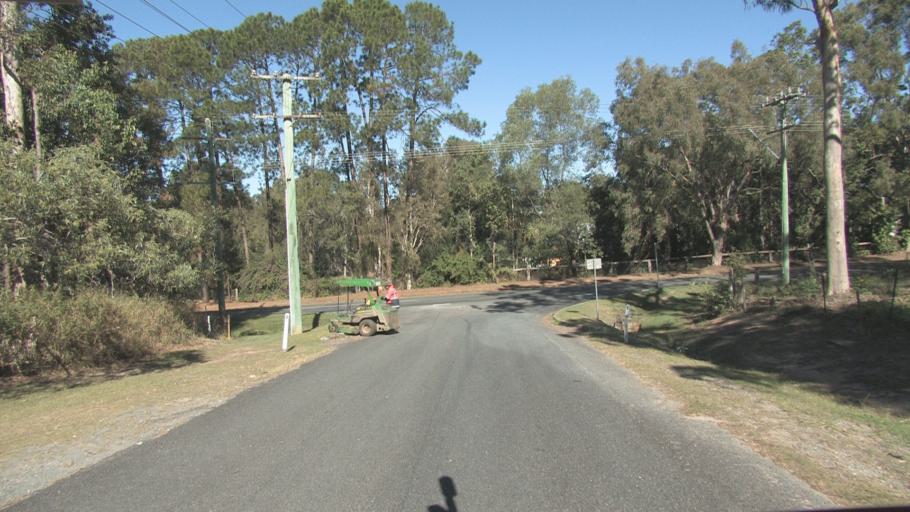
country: AU
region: Queensland
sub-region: Logan
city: Park Ridge South
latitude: -27.7162
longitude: 153.0403
